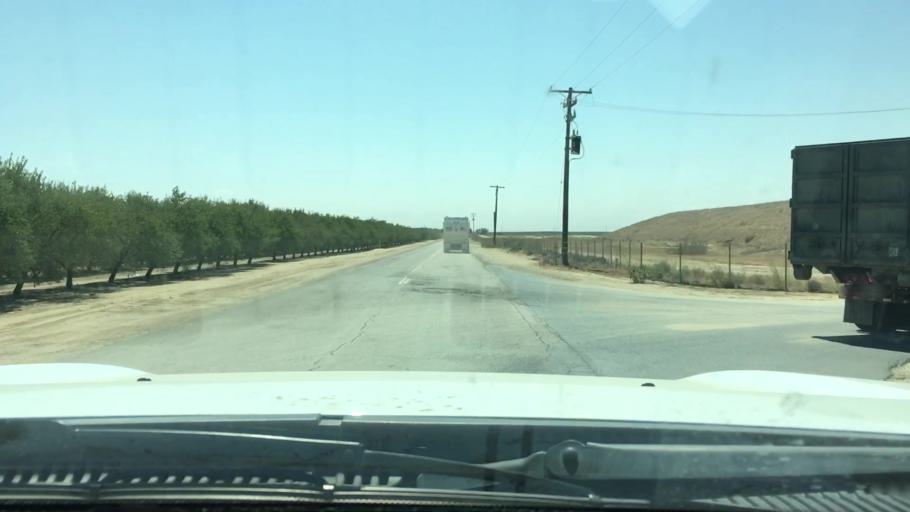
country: US
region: California
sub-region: Kern County
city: Wasco
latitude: 35.5148
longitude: -119.4033
